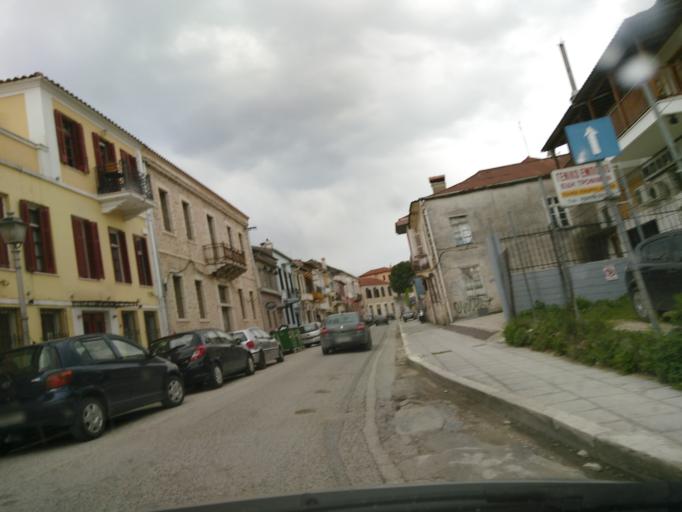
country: GR
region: Epirus
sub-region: Nomos Ioanninon
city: Ioannina
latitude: 39.6711
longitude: 20.8550
